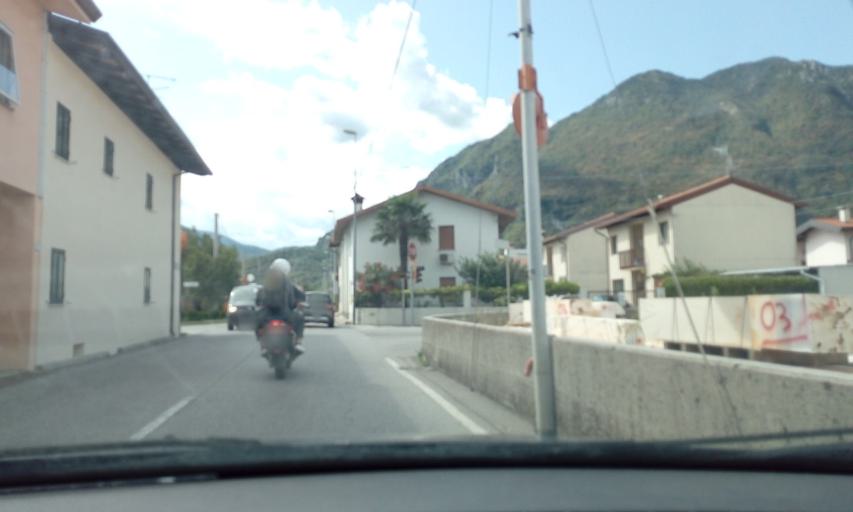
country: IT
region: Friuli Venezia Giulia
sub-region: Provincia di Udine
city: Gemona
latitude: 46.2814
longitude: 13.1067
